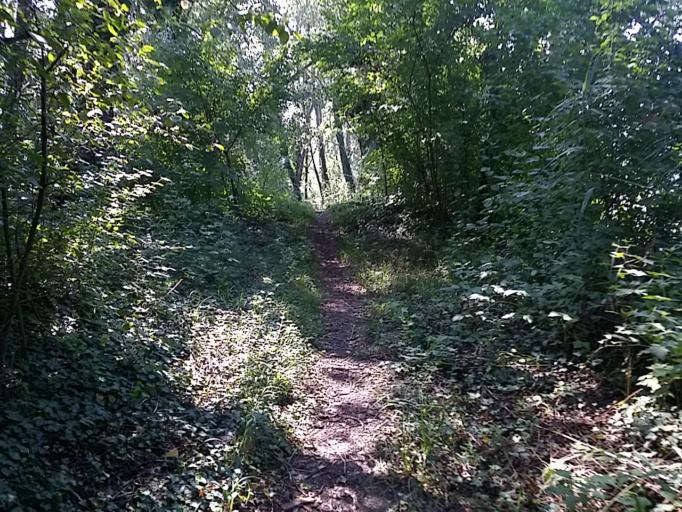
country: HR
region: Koprivnicko-Krizevacka
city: Ferdinandovac
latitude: 46.1157
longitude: 17.2011
